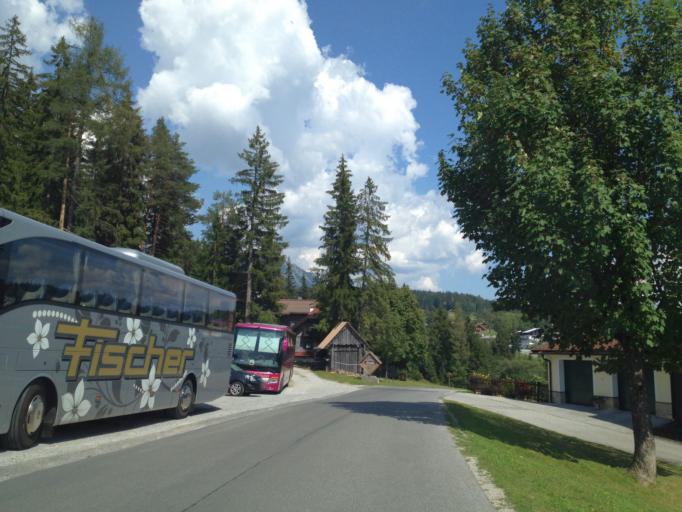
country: AT
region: Styria
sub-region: Politischer Bezirk Liezen
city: Schladming
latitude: 47.4063
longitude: 13.6260
